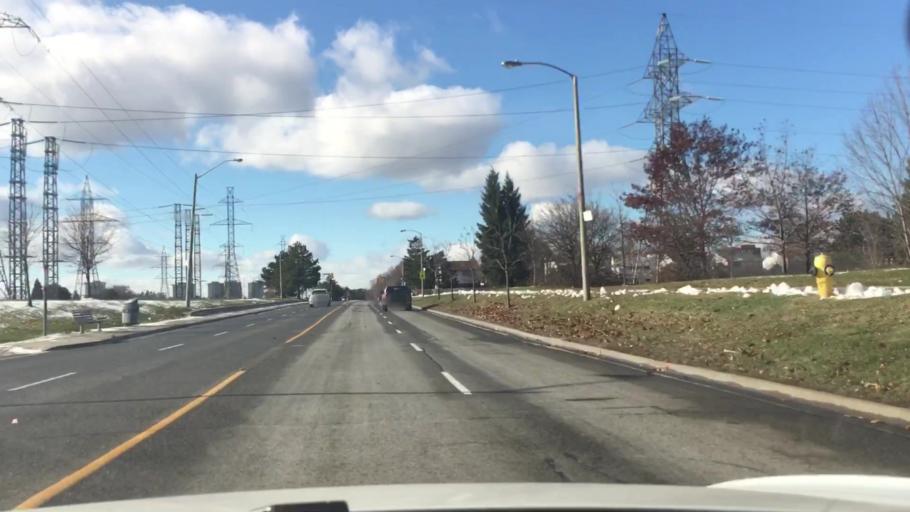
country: CA
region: Ontario
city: Scarborough
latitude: 43.8058
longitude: -79.3239
